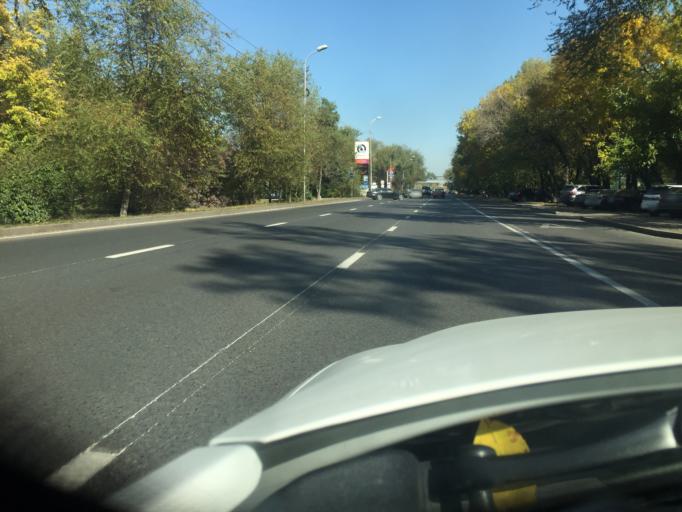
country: KZ
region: Almaty Qalasy
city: Almaty
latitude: 43.2623
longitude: 76.8968
